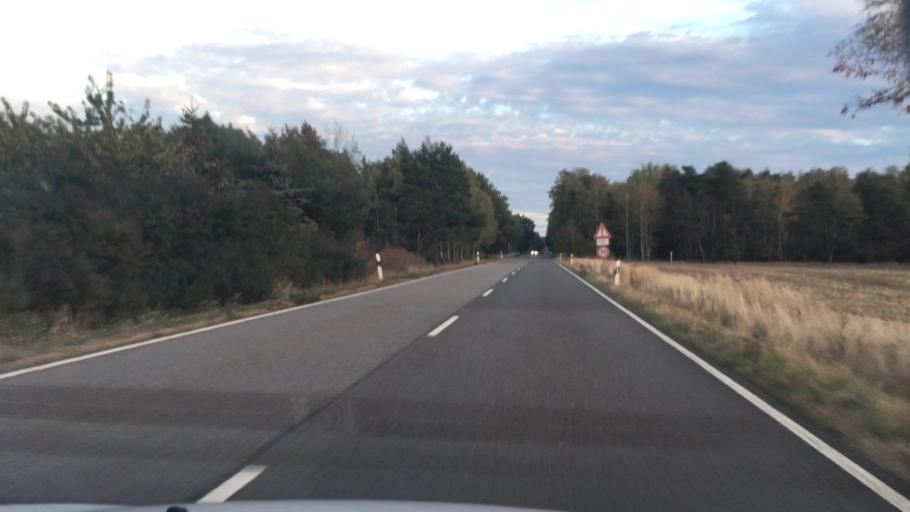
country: DE
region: Brandenburg
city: Welzow
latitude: 51.5701
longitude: 14.1007
